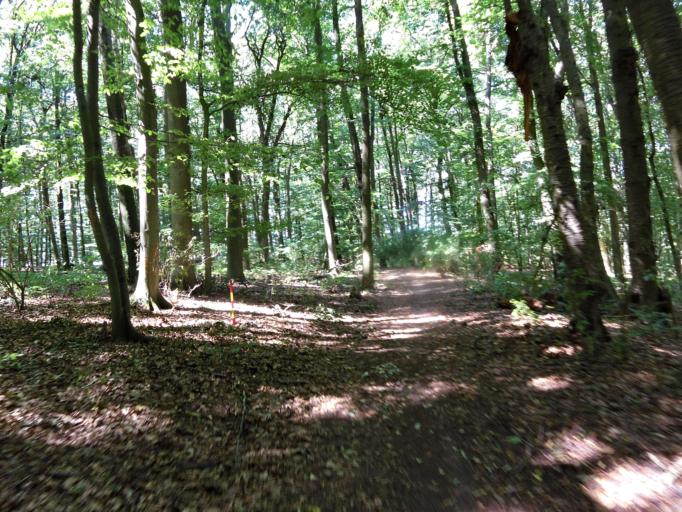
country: DE
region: Bavaria
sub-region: Regierungsbezirk Unterfranken
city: Theilheim
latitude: 49.7496
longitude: 10.0140
